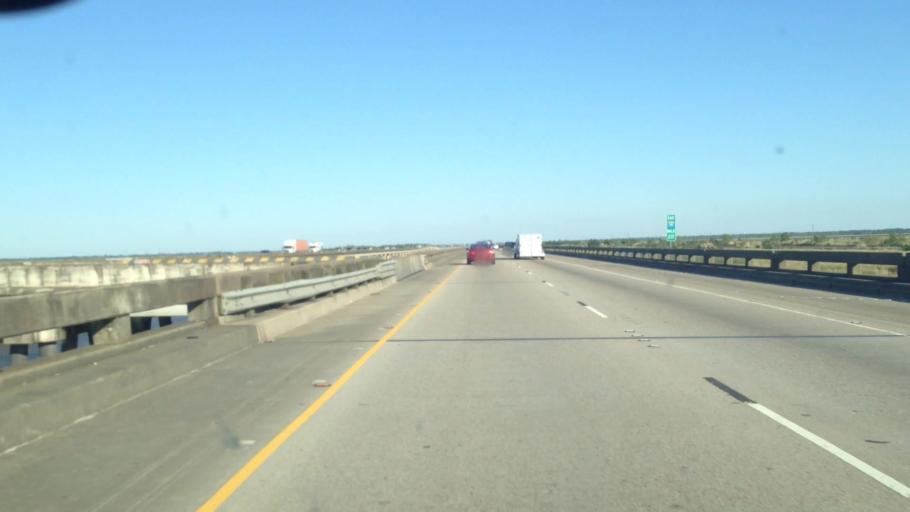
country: US
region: Louisiana
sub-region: Saint Charles Parish
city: New Sarpy
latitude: 30.0319
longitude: -90.3373
